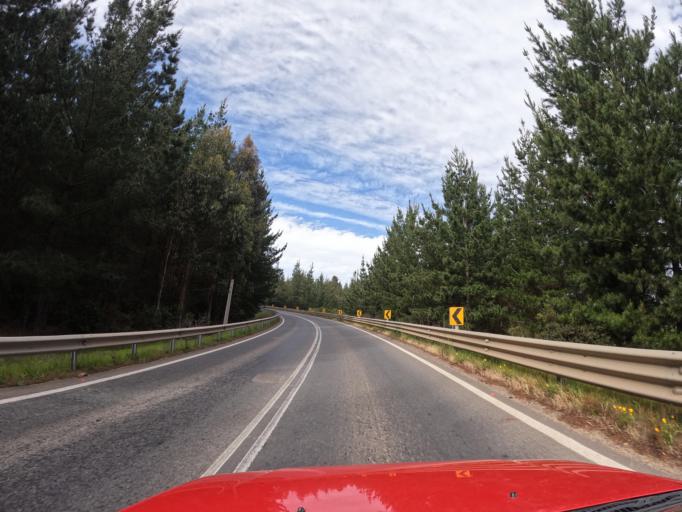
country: CL
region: O'Higgins
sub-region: Provincia de Colchagua
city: Santa Cruz
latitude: -34.3142
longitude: -71.8535
